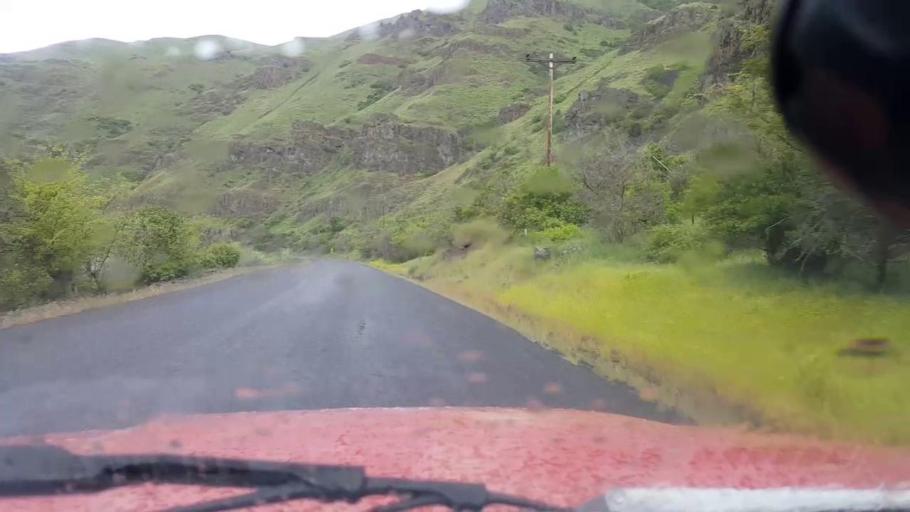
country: US
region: Washington
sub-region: Asotin County
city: Asotin
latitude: 46.0342
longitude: -117.3229
